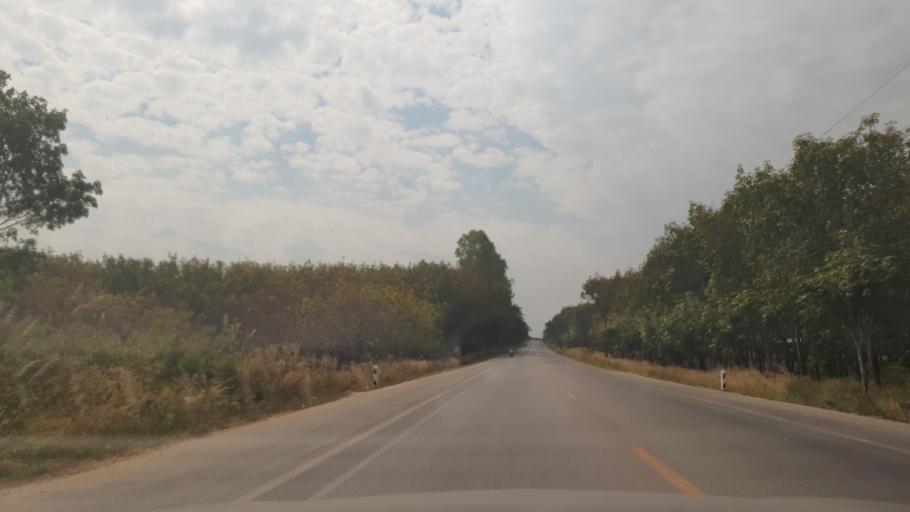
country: TH
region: Changwat Bueng Kan
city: Si Wilai
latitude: 18.2873
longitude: 103.7960
